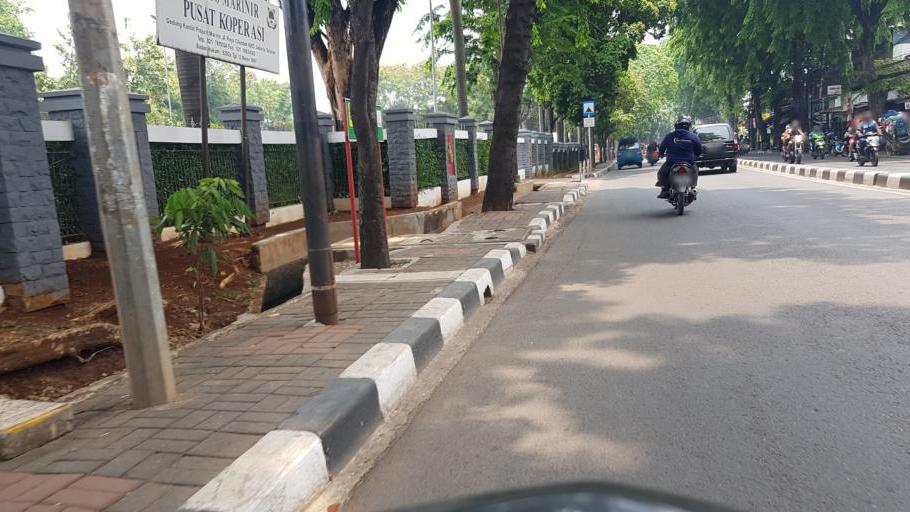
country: ID
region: West Java
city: Pamulang
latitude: -6.3002
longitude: 106.8144
